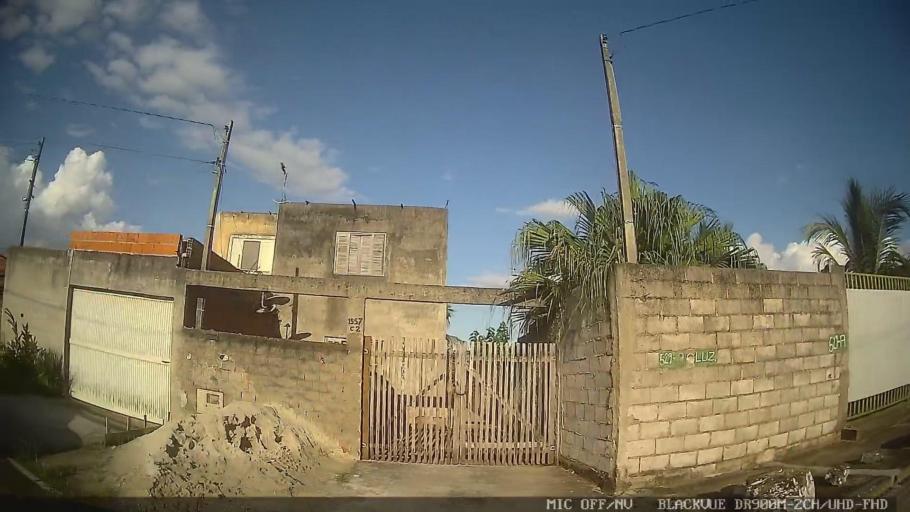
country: BR
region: Sao Paulo
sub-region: Caraguatatuba
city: Caraguatatuba
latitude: -23.6900
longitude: -45.4332
